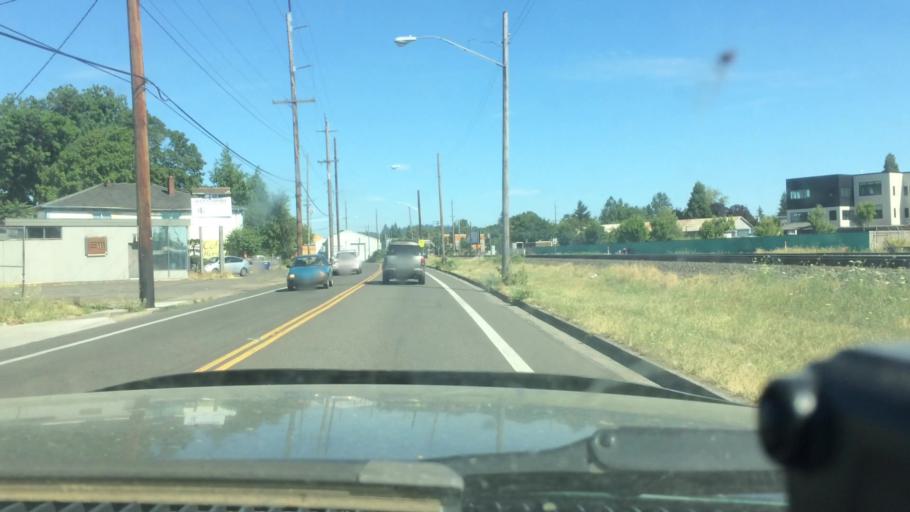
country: US
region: Oregon
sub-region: Lane County
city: Eugene
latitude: 44.0596
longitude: -123.1122
